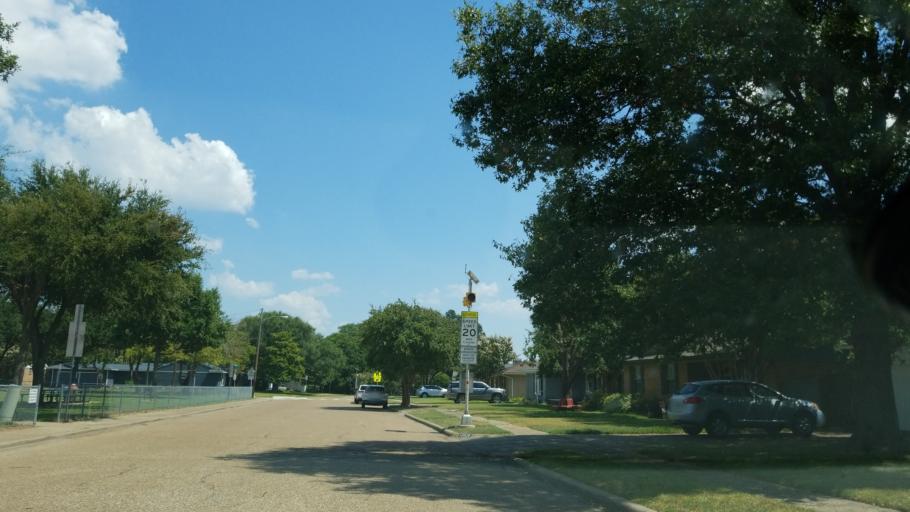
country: US
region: Texas
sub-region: Dallas County
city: Richardson
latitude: 32.8830
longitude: -96.7082
